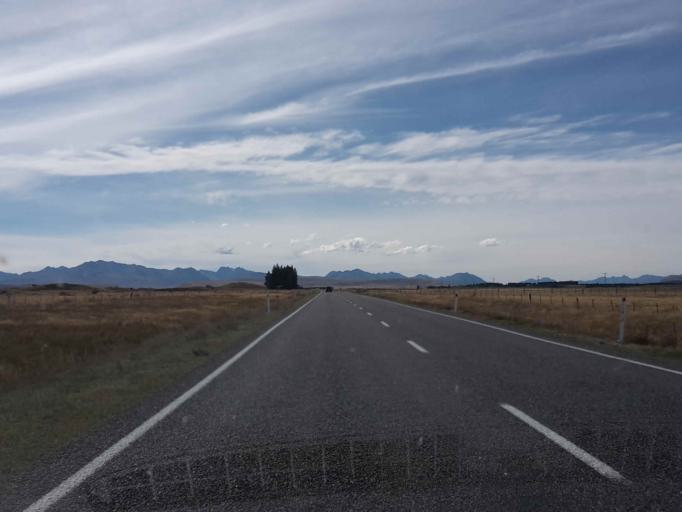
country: NZ
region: Canterbury
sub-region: Timaru District
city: Pleasant Point
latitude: -44.1271
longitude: 170.3505
